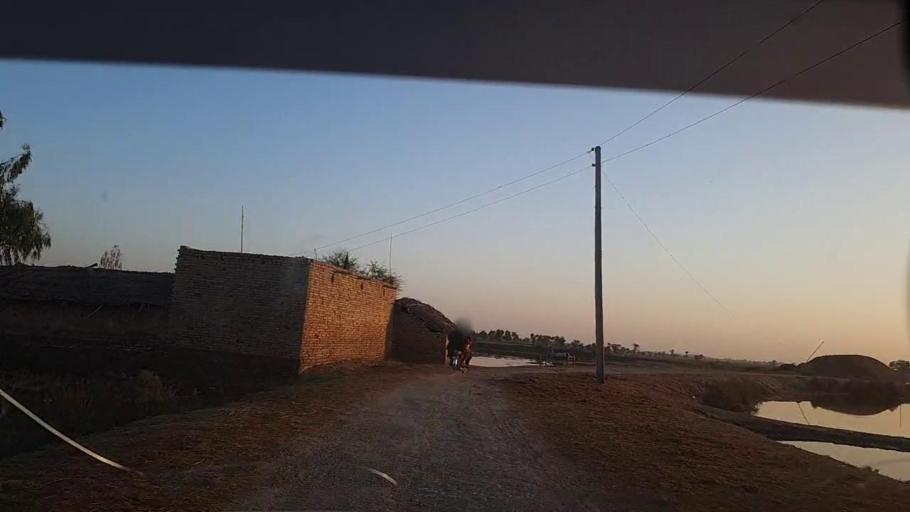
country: PK
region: Sindh
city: Ratodero
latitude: 27.8901
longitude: 68.2364
